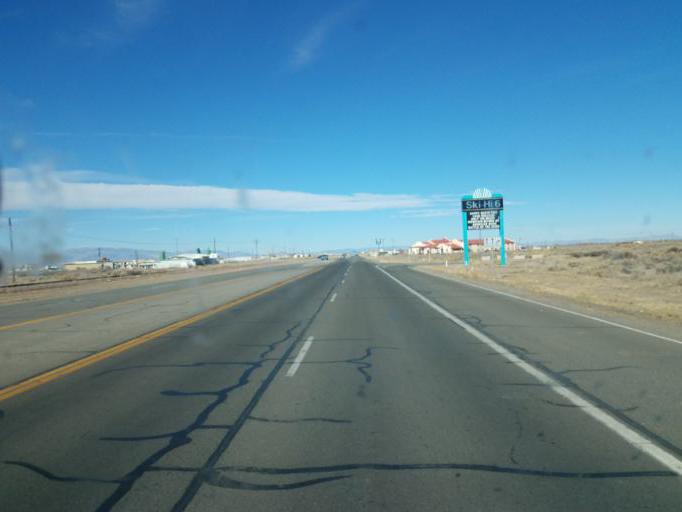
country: US
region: Colorado
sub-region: Alamosa County
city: Alamosa
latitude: 37.4814
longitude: -105.9092
